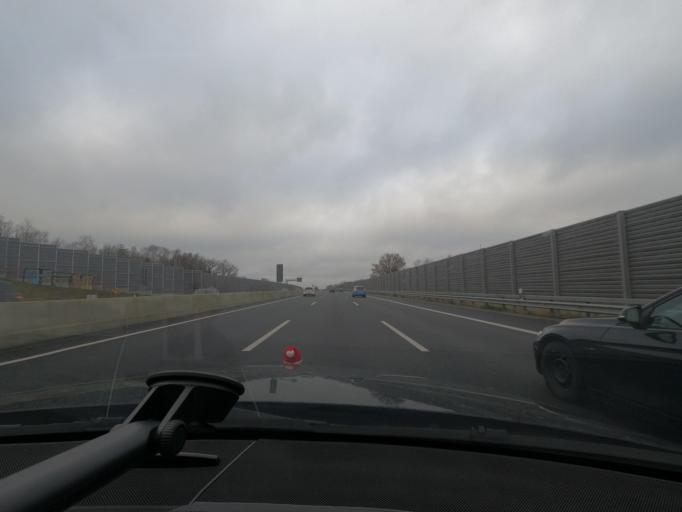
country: DE
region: Schleswig-Holstein
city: Ellerau
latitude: 53.7523
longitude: 9.9500
